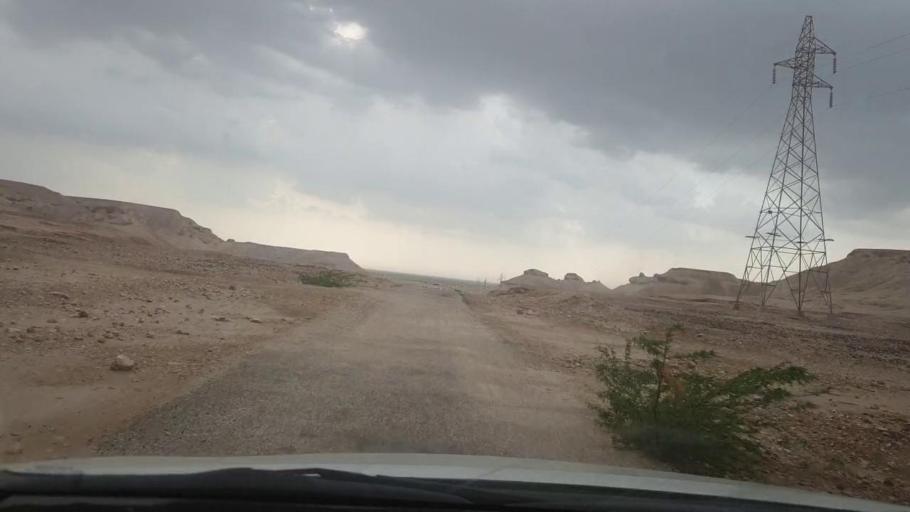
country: PK
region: Sindh
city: Khairpur
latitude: 27.4693
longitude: 68.9047
